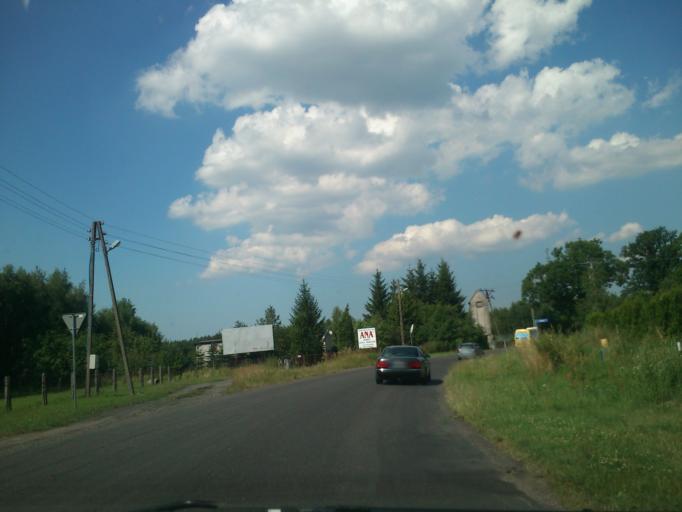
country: PL
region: West Pomeranian Voivodeship
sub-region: Powiat goleniowski
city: Goleniow
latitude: 53.5008
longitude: 14.7775
